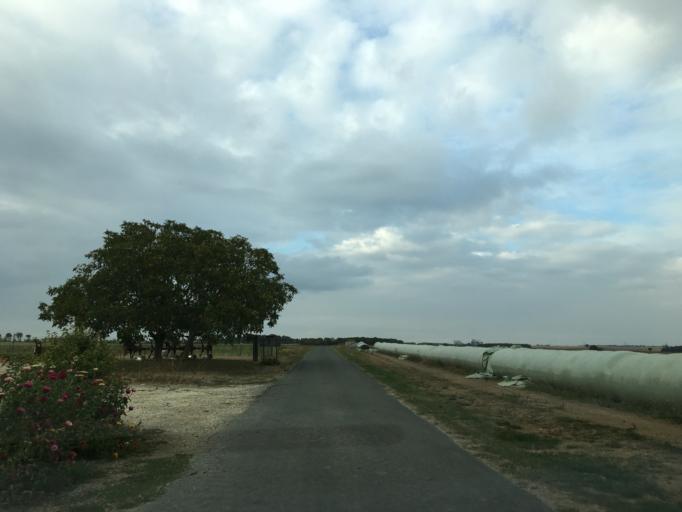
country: FR
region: Poitou-Charentes
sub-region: Departement des Deux-Sevres
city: Beauvoir-sur-Niort
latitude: 46.0795
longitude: -0.4981
